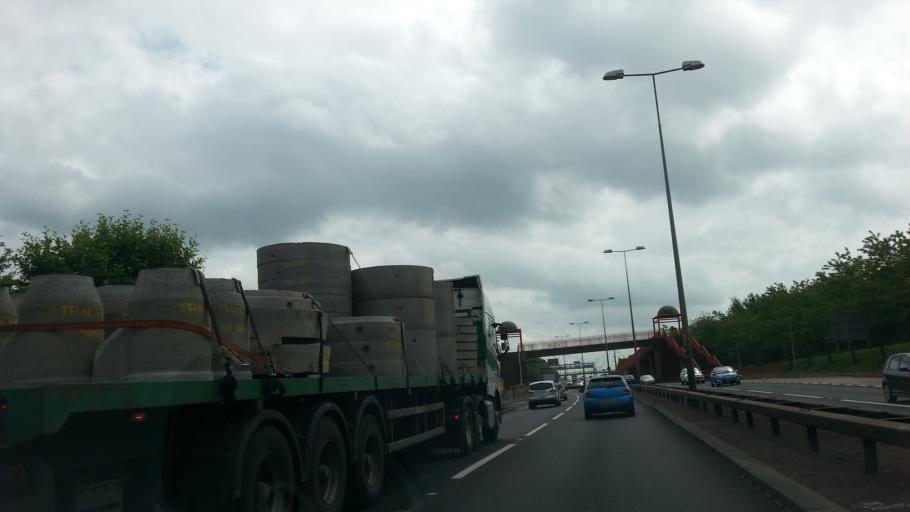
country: GB
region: England
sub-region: Staffordshire
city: Longton
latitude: 52.9812
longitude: -2.1146
